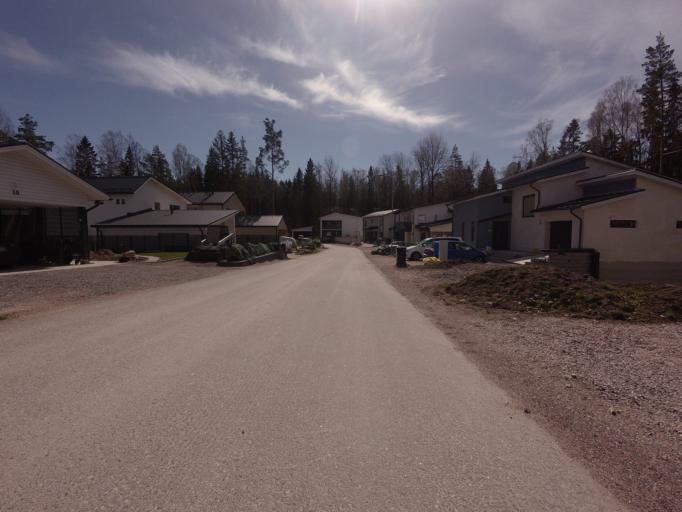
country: FI
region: Uusimaa
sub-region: Helsinki
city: Kauniainen
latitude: 60.1981
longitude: 24.7005
